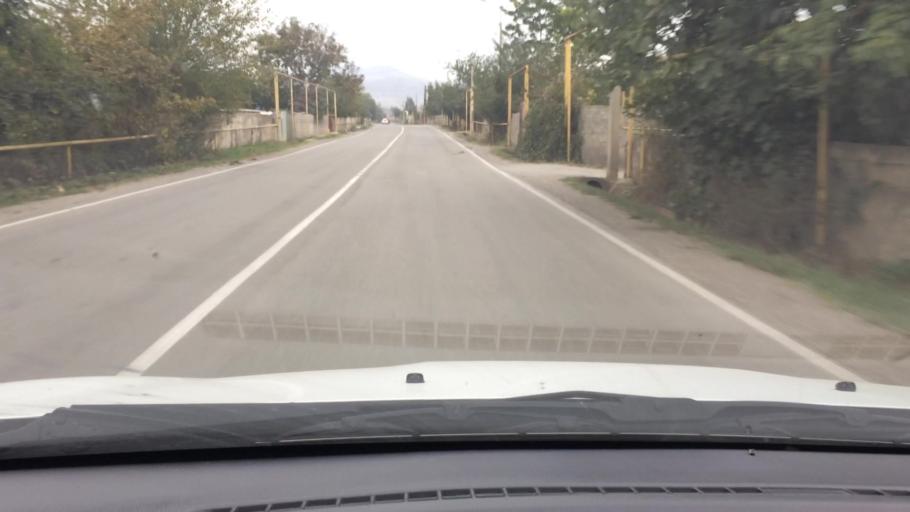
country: AM
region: Tavush
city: Bagratashen
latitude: 41.2394
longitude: 44.8018
